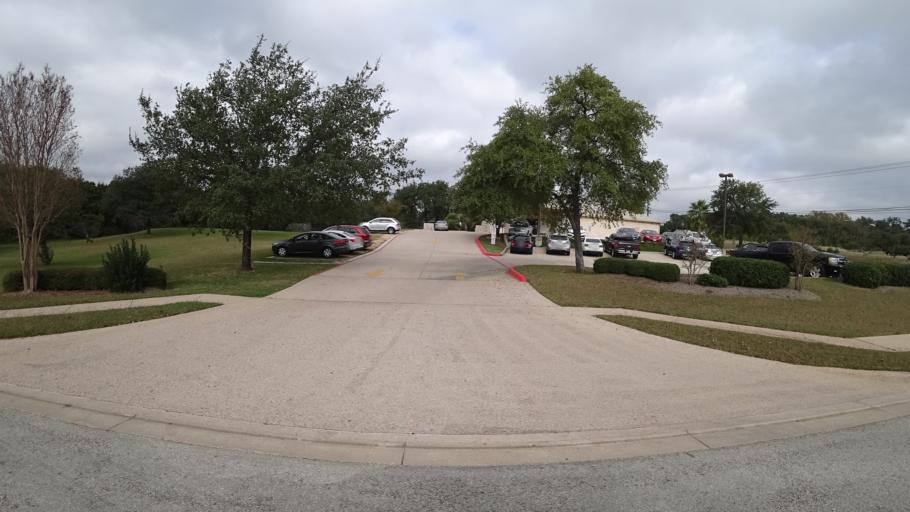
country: US
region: Texas
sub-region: Travis County
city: Barton Creek
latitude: 30.2569
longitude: -97.9051
